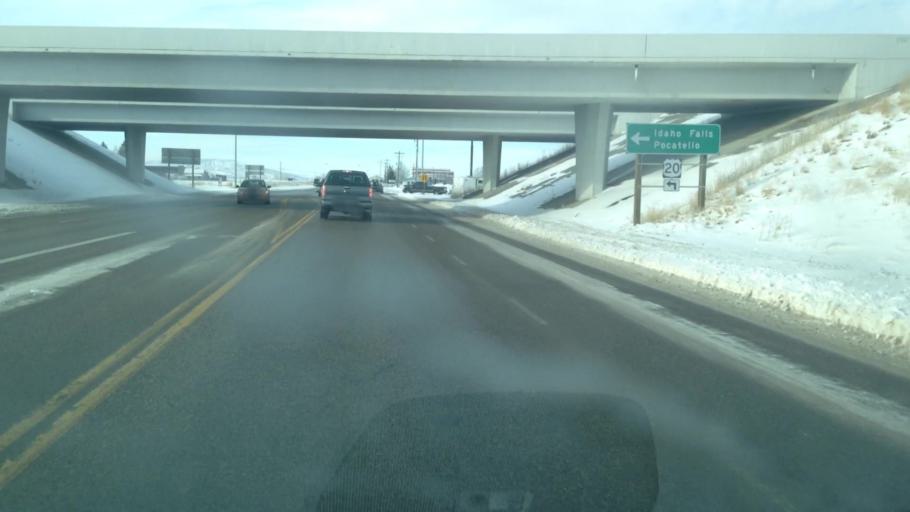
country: US
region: Idaho
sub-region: Madison County
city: Rexburg
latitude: 43.8046
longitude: -111.8125
